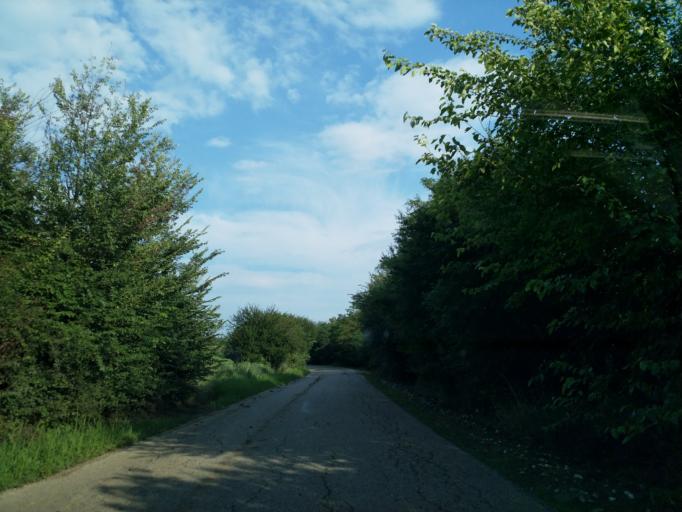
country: RS
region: Central Serbia
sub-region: Pomoravski Okrug
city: Jagodina
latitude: 43.9940
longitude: 21.1983
